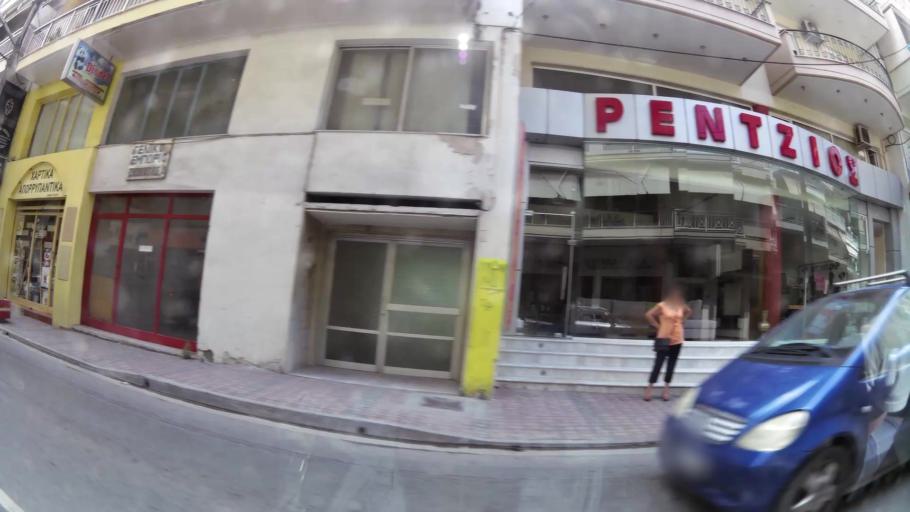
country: GR
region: Central Macedonia
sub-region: Nomos Pierias
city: Katerini
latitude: 40.2699
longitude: 22.5119
